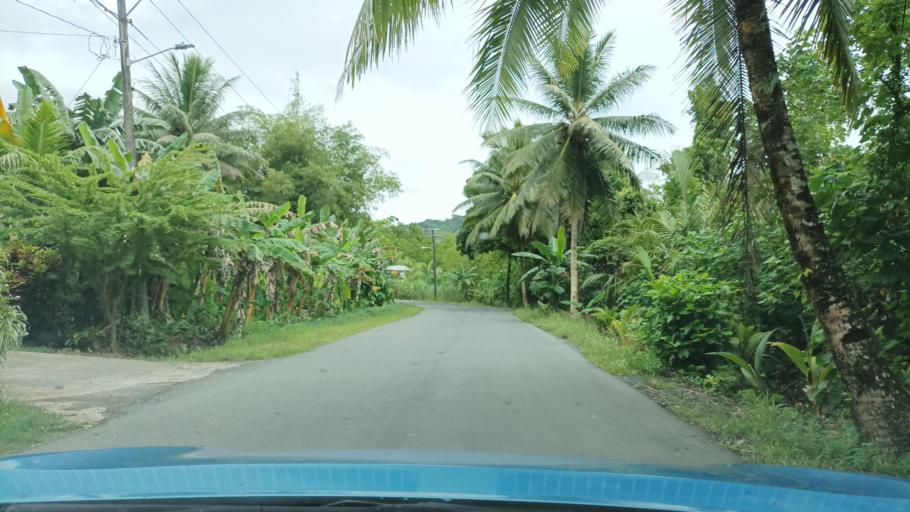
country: FM
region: Pohnpei
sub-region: Kolonia Municipality
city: Kolonia
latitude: 6.9394
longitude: 158.2779
